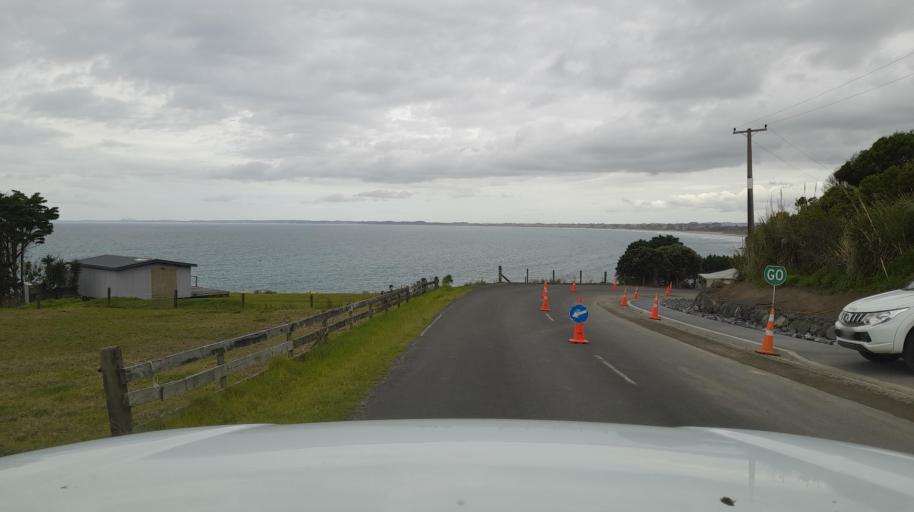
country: NZ
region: Northland
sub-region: Far North District
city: Ahipara
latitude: -35.1802
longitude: 173.1277
